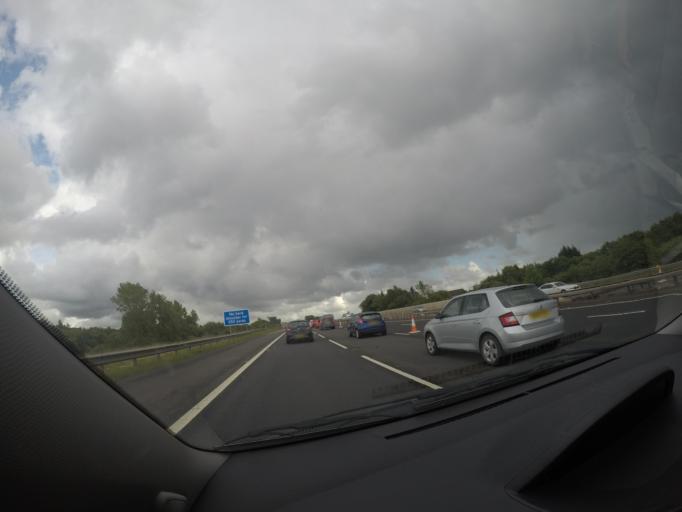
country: GB
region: Scotland
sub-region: South Lanarkshire
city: Uddingston
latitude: 55.8244
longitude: -4.0763
